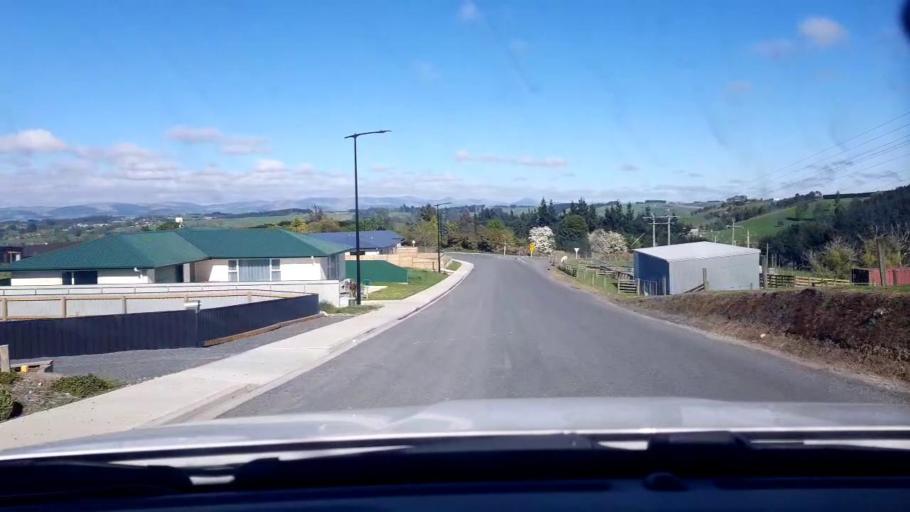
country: NZ
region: Otago
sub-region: Clutha District
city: Balclutha
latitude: -46.2238
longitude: 169.7484
